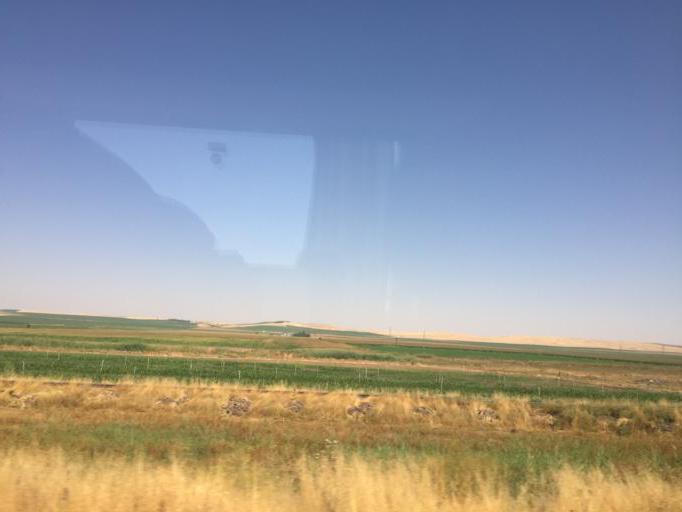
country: TR
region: Diyarbakir
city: Tepe
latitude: 37.8500
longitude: 40.7807
